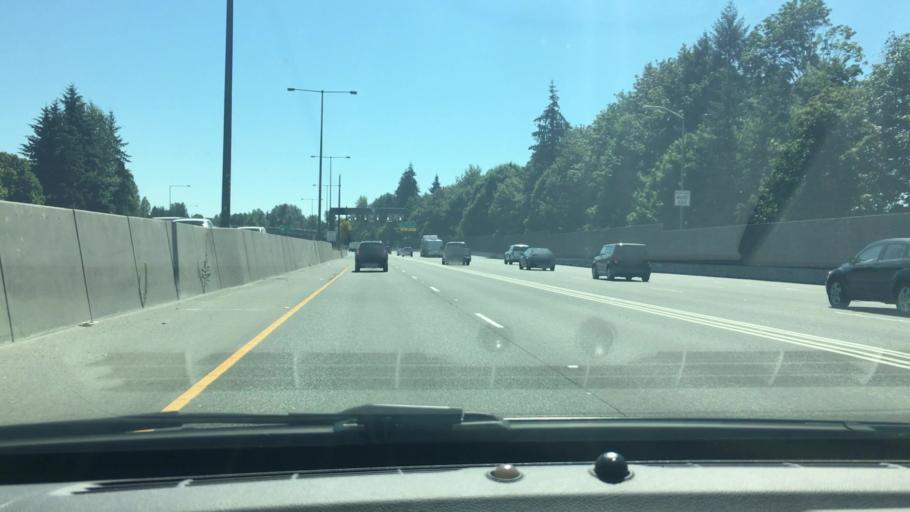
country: US
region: Washington
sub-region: King County
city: Kirkland
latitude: 47.6740
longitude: -122.1866
